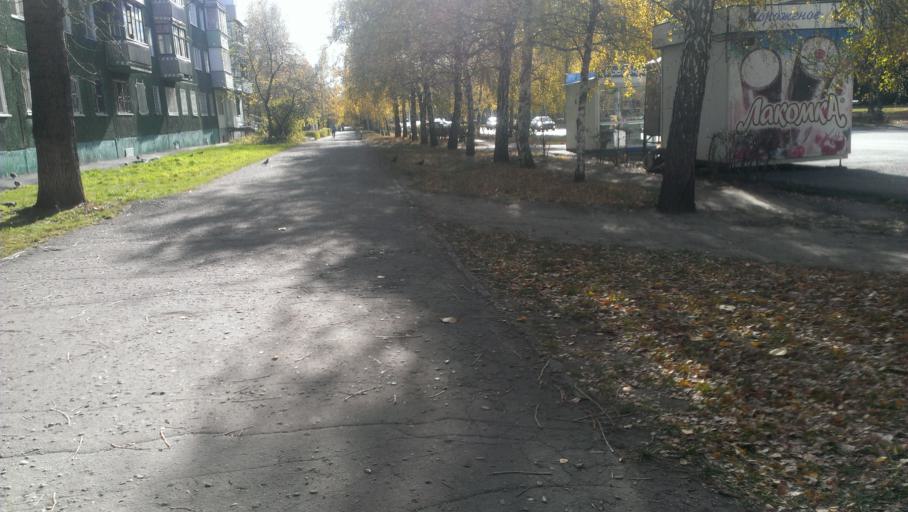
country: RU
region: Altai Krai
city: Novosilikatnyy
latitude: 53.3539
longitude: 83.6845
